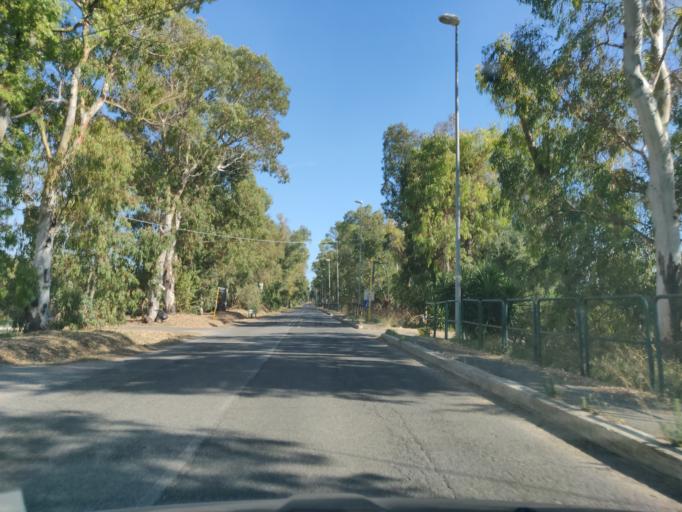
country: IT
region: Latium
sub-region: Citta metropolitana di Roma Capitale
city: Aurelia
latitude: 42.1359
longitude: 11.7693
